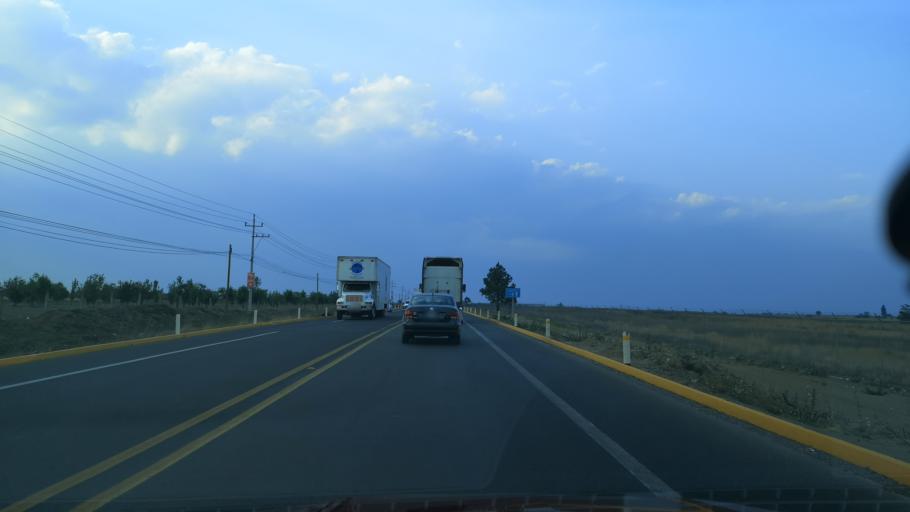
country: MX
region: Puebla
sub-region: Juan C. Bonilla
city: Santa Maria Zacatepec
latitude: 19.1453
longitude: -98.3741
